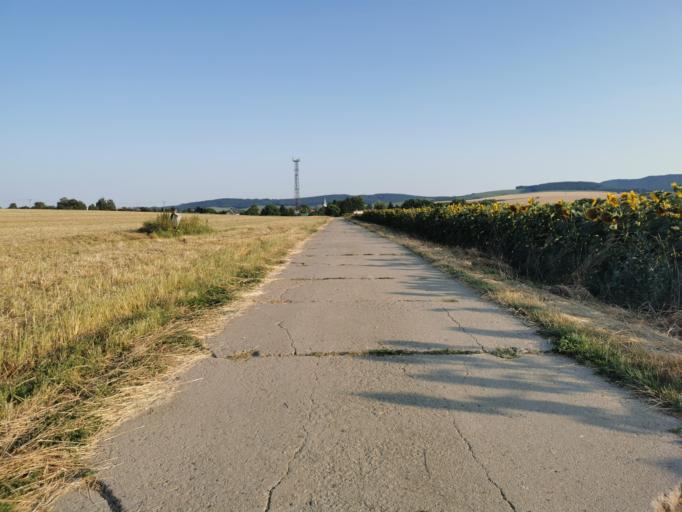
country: SK
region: Trnavsky
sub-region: Okres Skalica
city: Skalica
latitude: 48.7792
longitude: 17.2792
